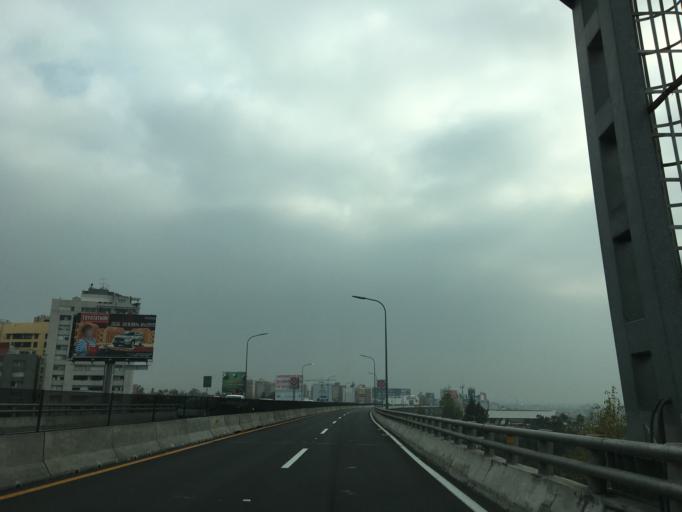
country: MX
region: Mexico City
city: Tlalpan
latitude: 19.3032
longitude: -99.1825
